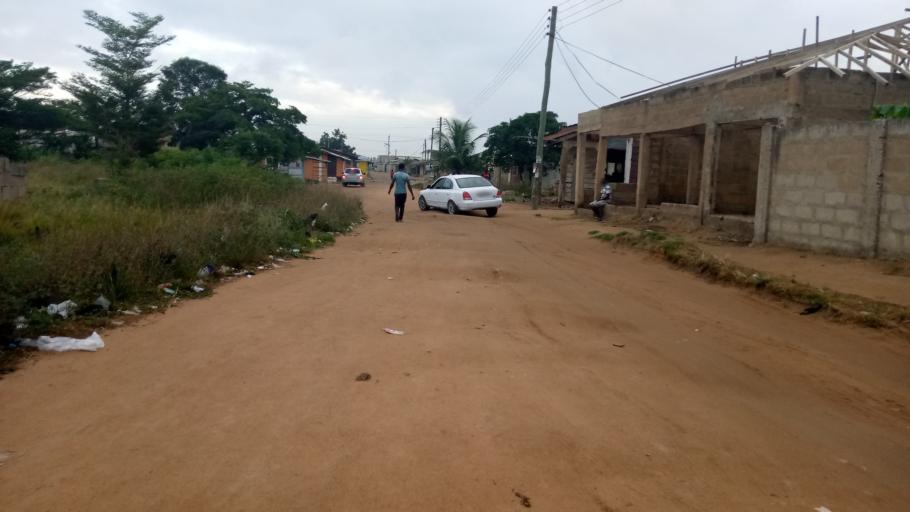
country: GH
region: Central
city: Kasoa
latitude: 5.5012
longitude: -0.4103
